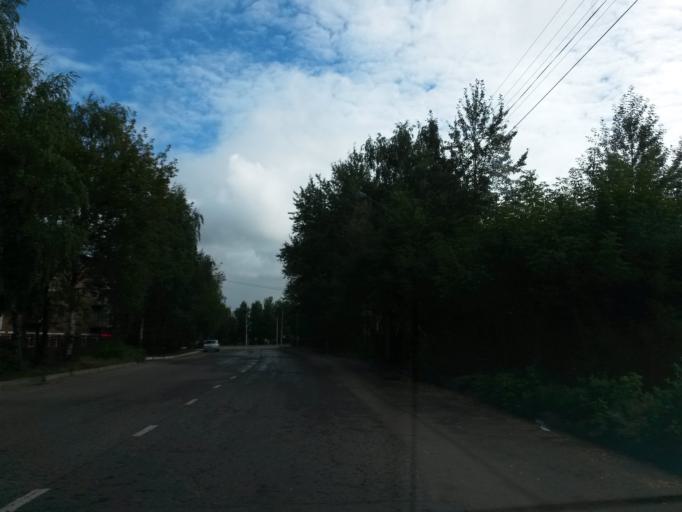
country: RU
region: Jaroslavl
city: Yaroslavl
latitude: 57.6452
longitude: 39.8777
